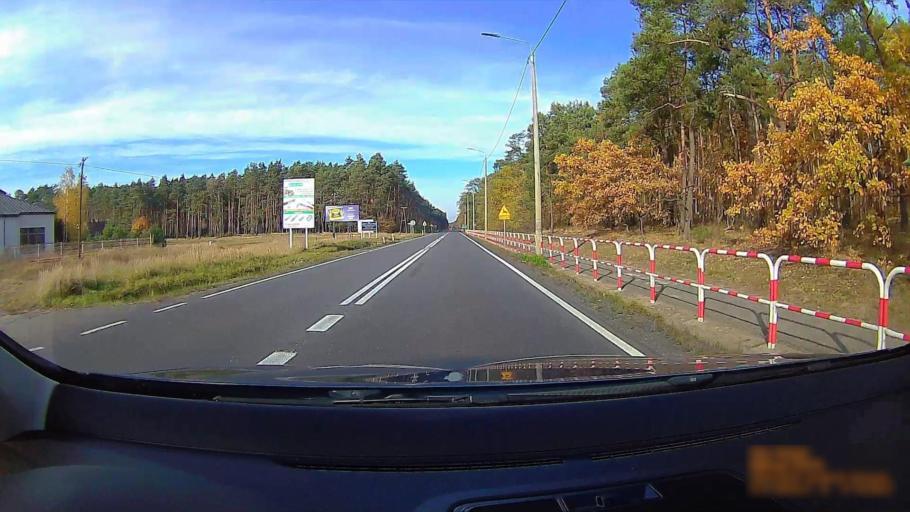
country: PL
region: Greater Poland Voivodeship
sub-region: Powiat ostrzeszowski
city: Ostrzeszow
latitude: 51.4461
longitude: 17.9109
